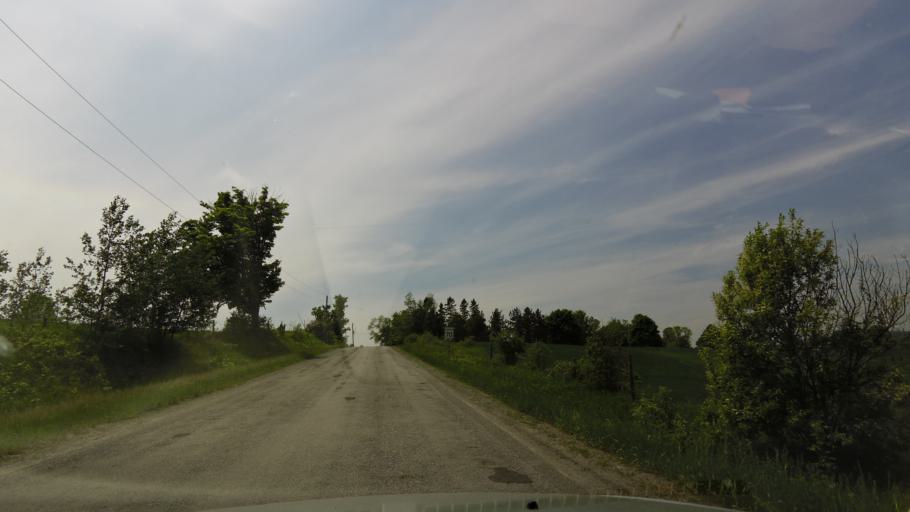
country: CA
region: Ontario
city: Omemee
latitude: 43.9764
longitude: -78.4982
